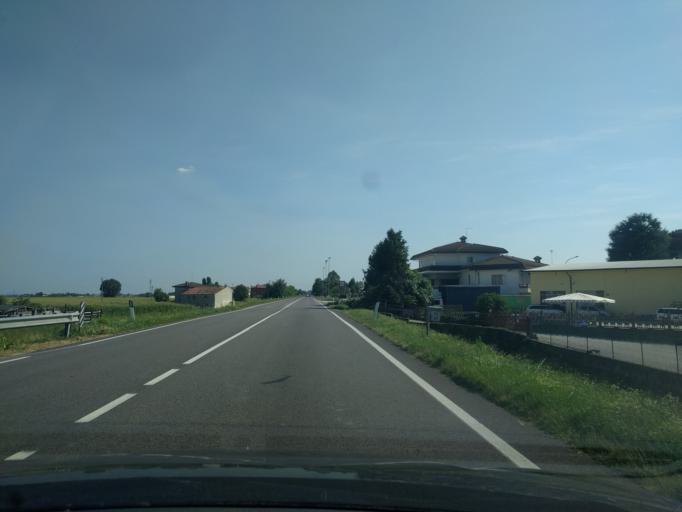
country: IT
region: Veneto
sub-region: Provincia di Padova
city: Solesino
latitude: 45.1731
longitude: 11.7563
